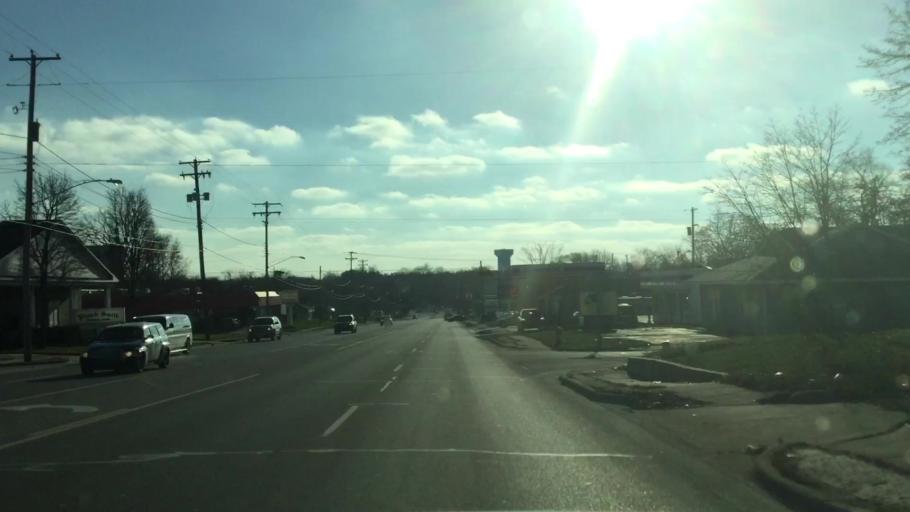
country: US
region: Michigan
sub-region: Genesee County
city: Flint
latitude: 43.0232
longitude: -83.7326
